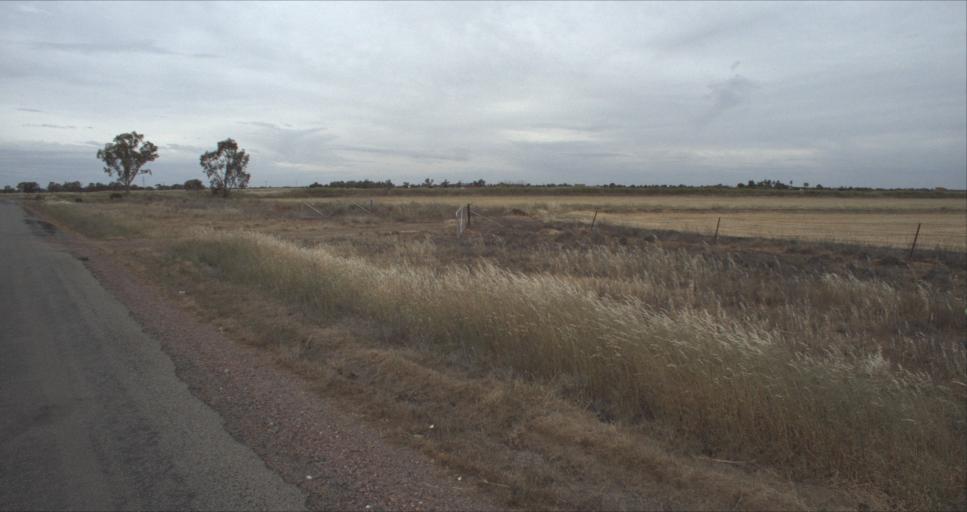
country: AU
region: New South Wales
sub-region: Leeton
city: Leeton
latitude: -34.4826
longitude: 146.4011
